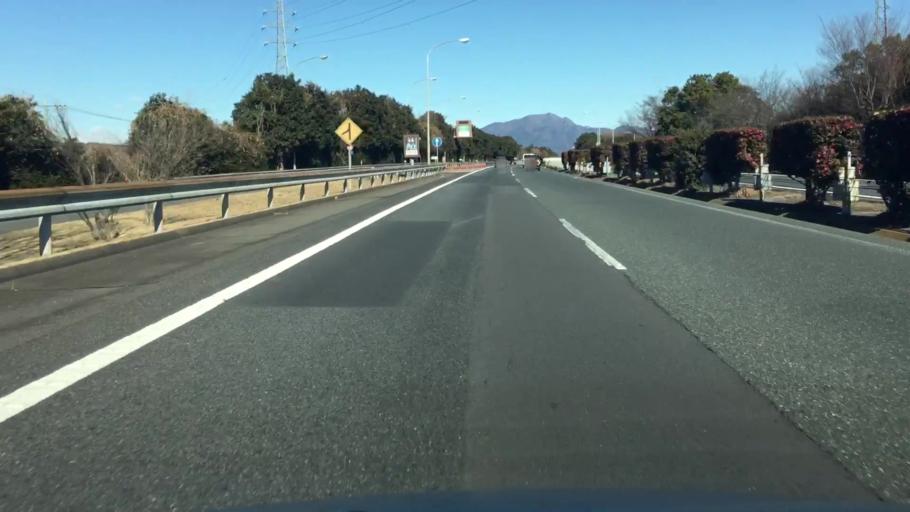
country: JP
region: Gunma
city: Kanekomachi
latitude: 36.4317
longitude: 139.0148
